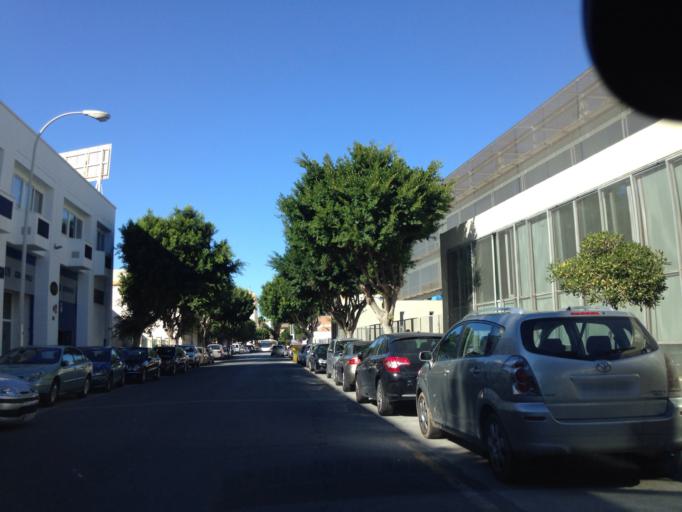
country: ES
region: Andalusia
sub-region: Provincia de Malaga
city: Malaga
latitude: 36.6881
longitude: -4.4457
